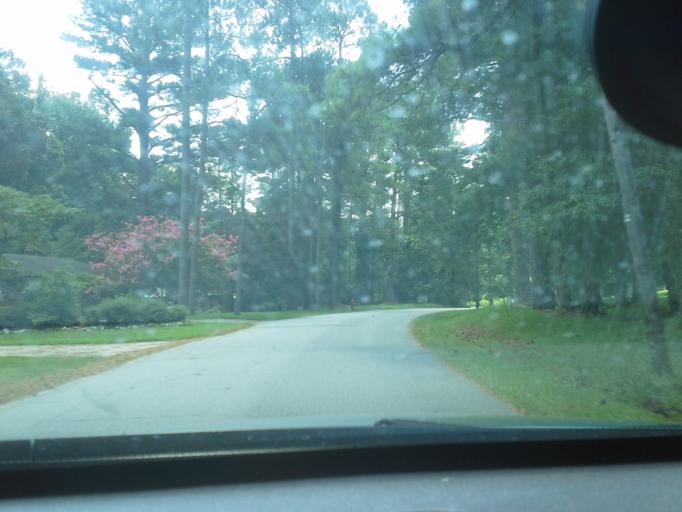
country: US
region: North Carolina
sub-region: Washington County
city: Plymouth
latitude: 35.8572
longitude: -76.7586
